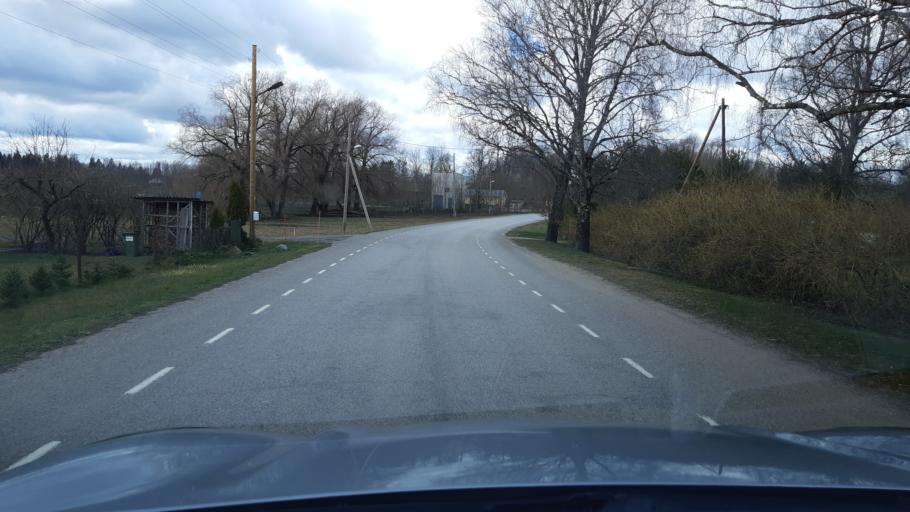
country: EE
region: Raplamaa
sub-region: Kehtna vald
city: Kehtna
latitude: 59.0419
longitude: 25.1216
